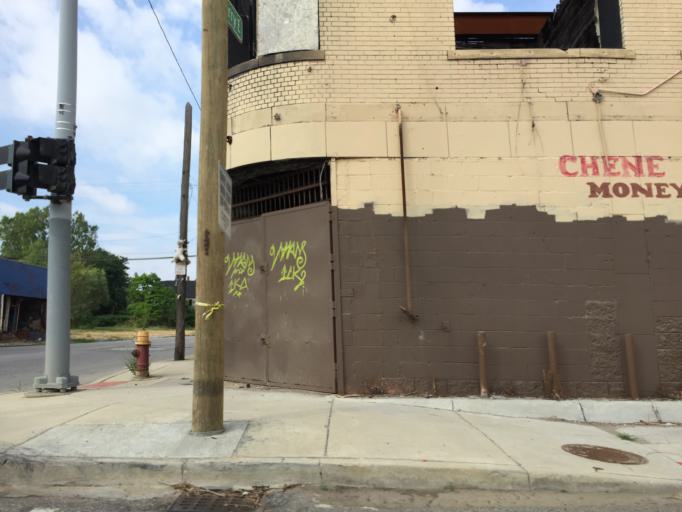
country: US
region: Michigan
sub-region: Wayne County
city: Hamtramck
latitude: 42.3700
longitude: -83.0437
